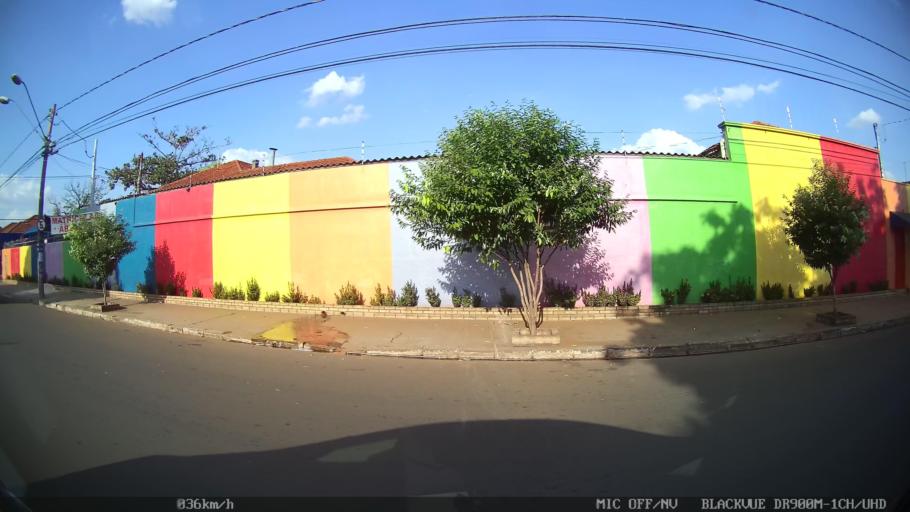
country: BR
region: Sao Paulo
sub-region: Ribeirao Preto
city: Ribeirao Preto
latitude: -21.1587
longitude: -47.8074
